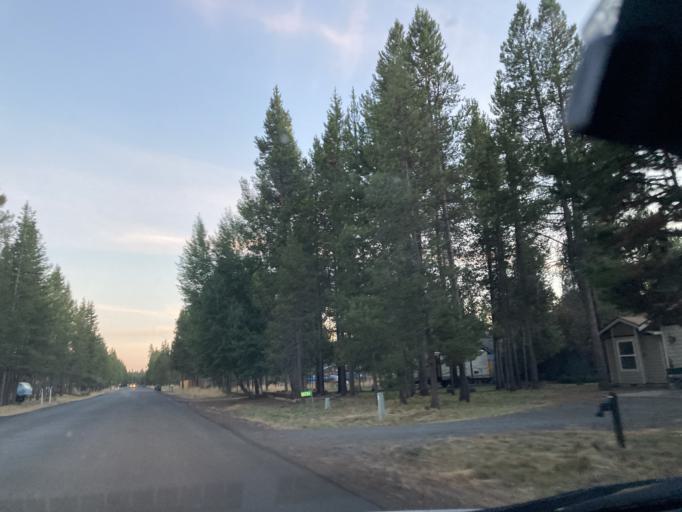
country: US
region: Oregon
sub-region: Deschutes County
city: Three Rivers
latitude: 43.8246
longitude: -121.4656
